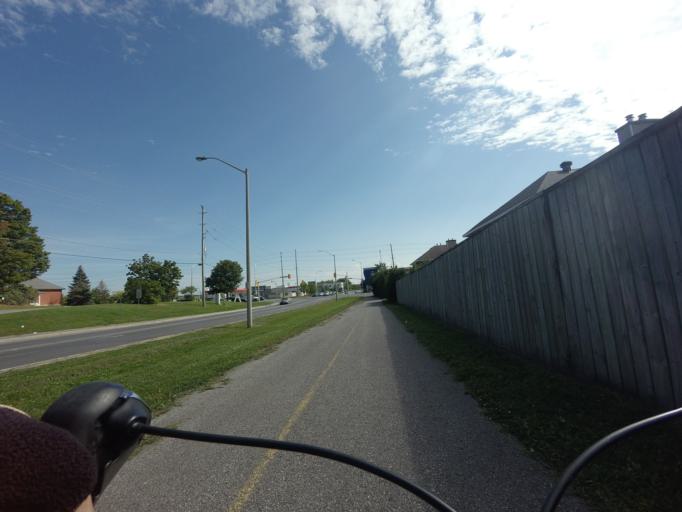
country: CA
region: Ontario
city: Bells Corners
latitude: 45.2693
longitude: -75.7518
